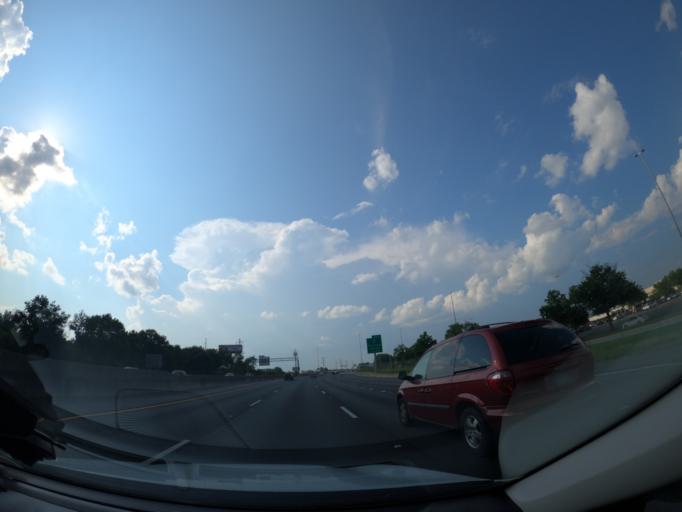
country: US
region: Georgia
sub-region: Columbia County
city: Martinez
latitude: 33.4609
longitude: -82.0801
